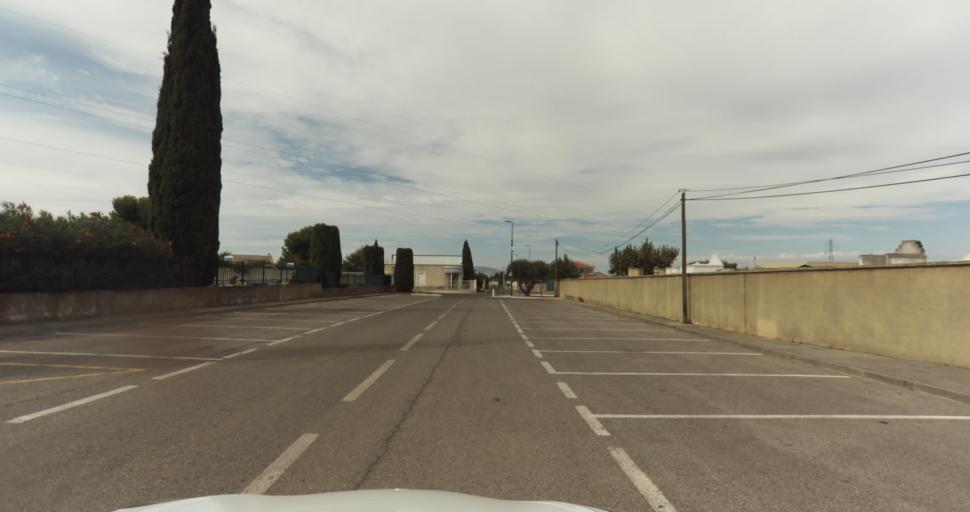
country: FR
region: Provence-Alpes-Cote d'Azur
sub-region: Departement des Bouches-du-Rhone
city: Miramas
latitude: 43.5744
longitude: 5.0089
